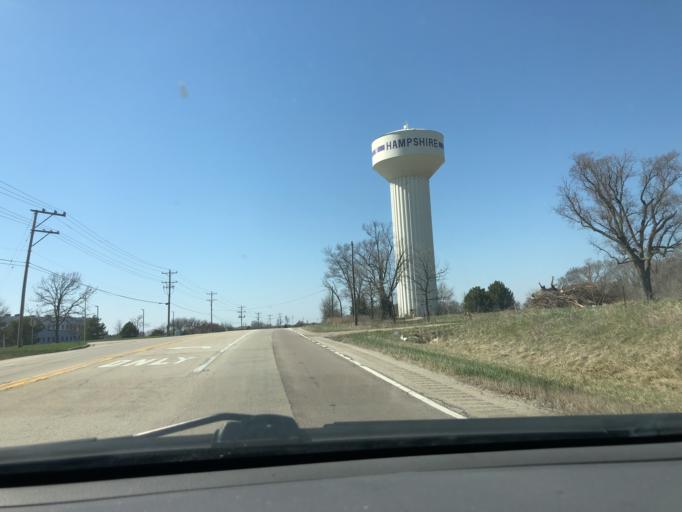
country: US
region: Illinois
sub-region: Kane County
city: Hampshire
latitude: 42.1352
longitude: -88.4996
